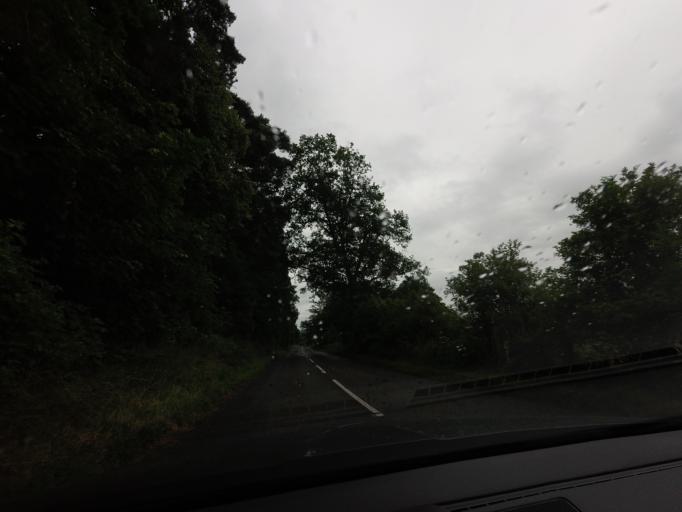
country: GB
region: Scotland
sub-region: Aberdeenshire
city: Turriff
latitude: 57.5389
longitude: -2.4957
